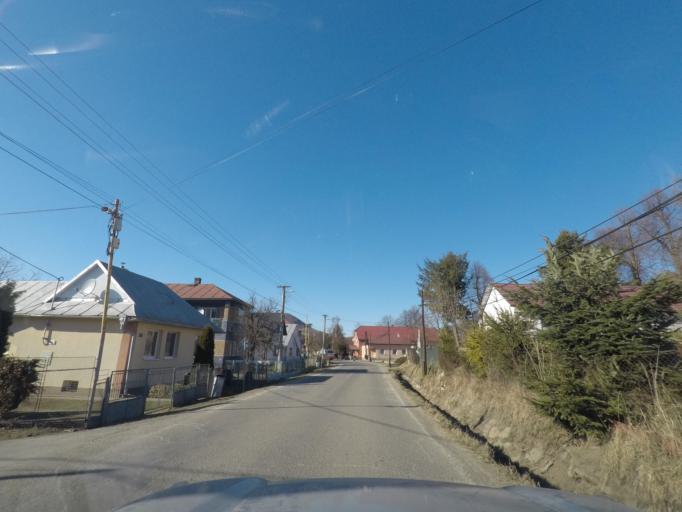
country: SK
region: Presovsky
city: Snina
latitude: 49.0662
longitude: 22.1709
